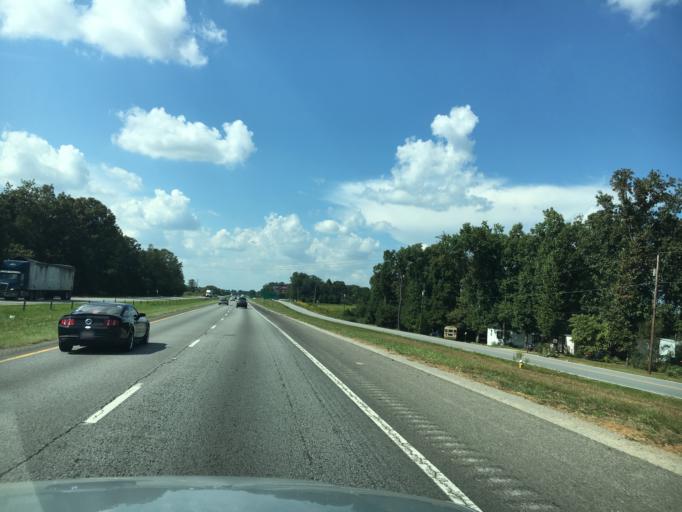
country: US
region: South Carolina
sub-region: Greenville County
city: Fountain Inn
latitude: 34.6507
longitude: -82.1571
